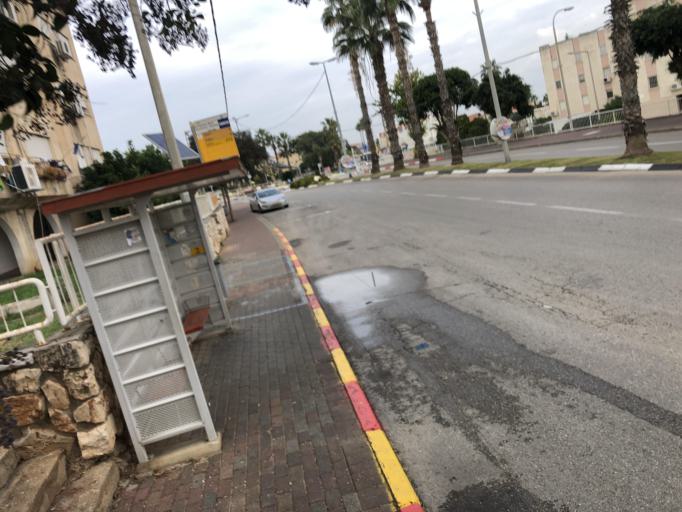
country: IL
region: Northern District
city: `Akko
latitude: 32.9318
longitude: 35.0925
